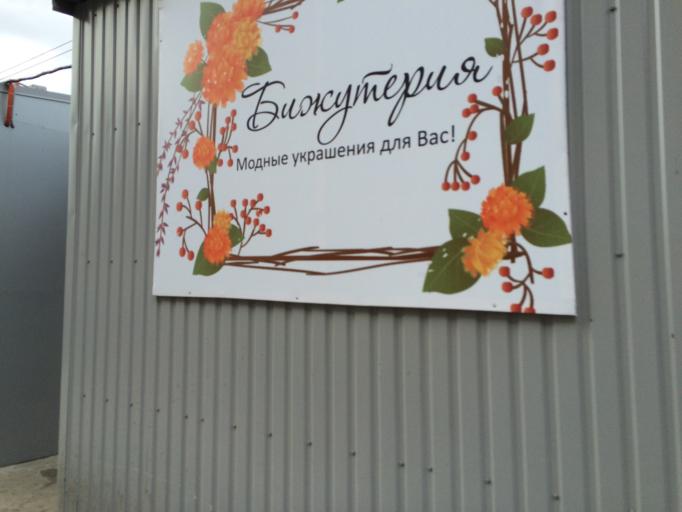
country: RU
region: Chelyabinsk
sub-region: Gorod Magnitogorsk
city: Magnitogorsk
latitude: 53.3992
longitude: 58.9786
